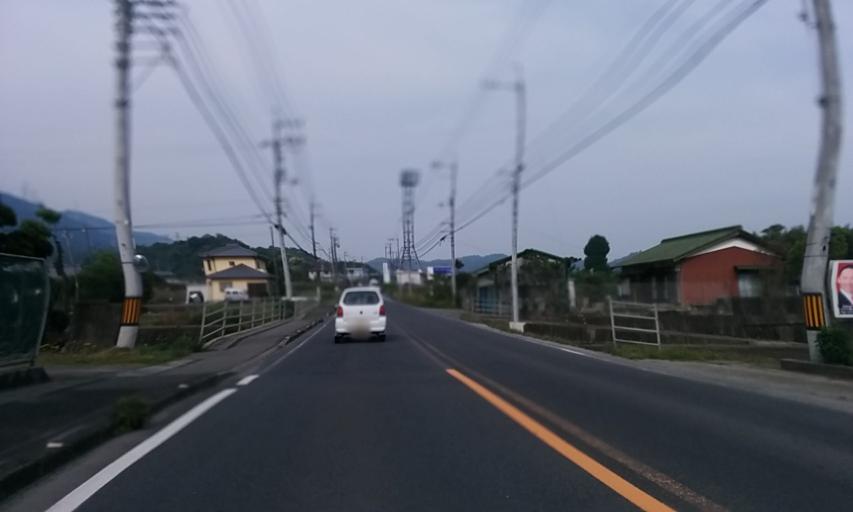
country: JP
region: Ehime
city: Niihama
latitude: 33.9528
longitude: 133.4135
